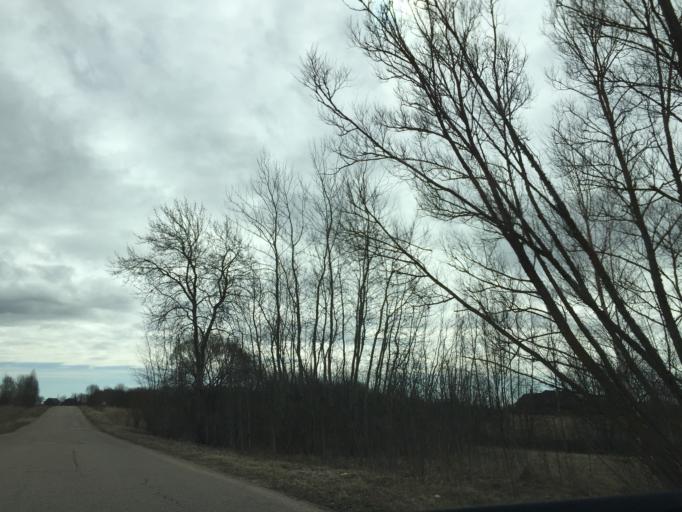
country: LV
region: Daugavpils
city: Daugavpils
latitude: 55.9249
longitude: 26.7330
